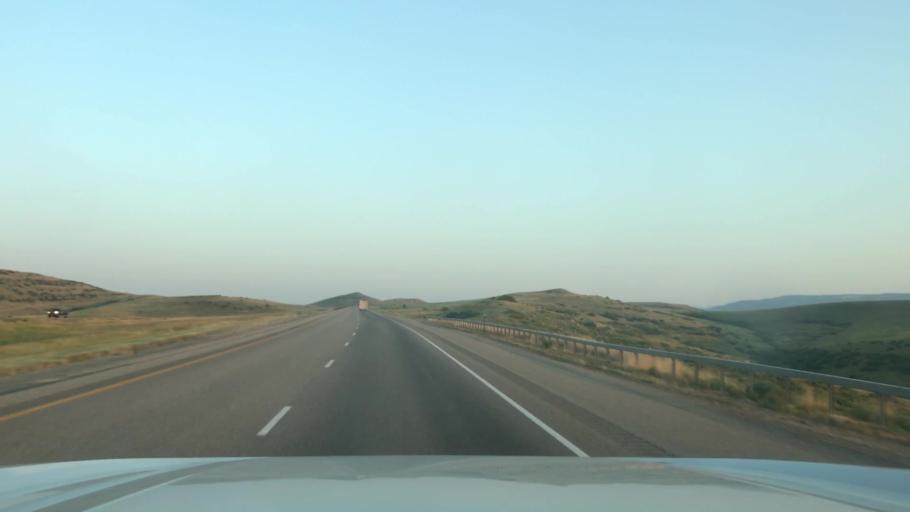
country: US
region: Wyoming
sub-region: Sheridan County
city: Sheridan
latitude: 44.7192
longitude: -106.9163
